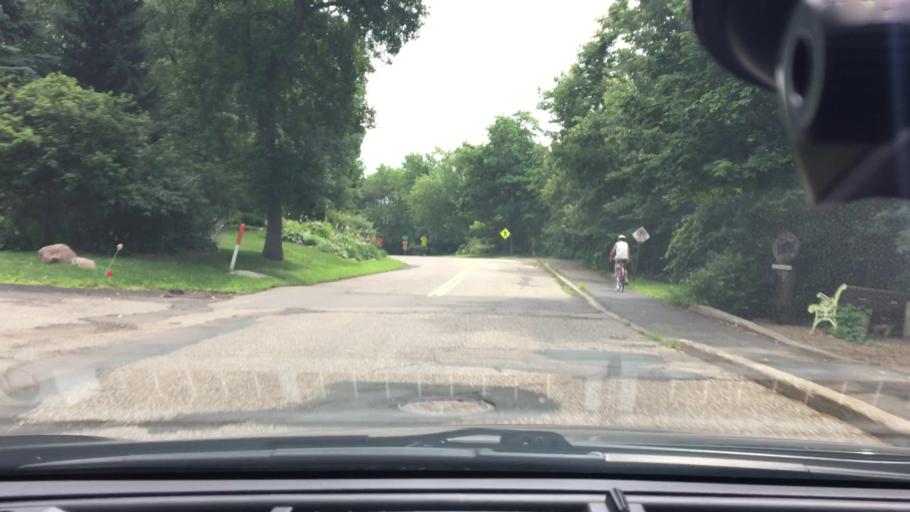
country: US
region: Minnesota
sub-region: Hennepin County
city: New Hope
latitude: 45.0134
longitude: -93.4159
